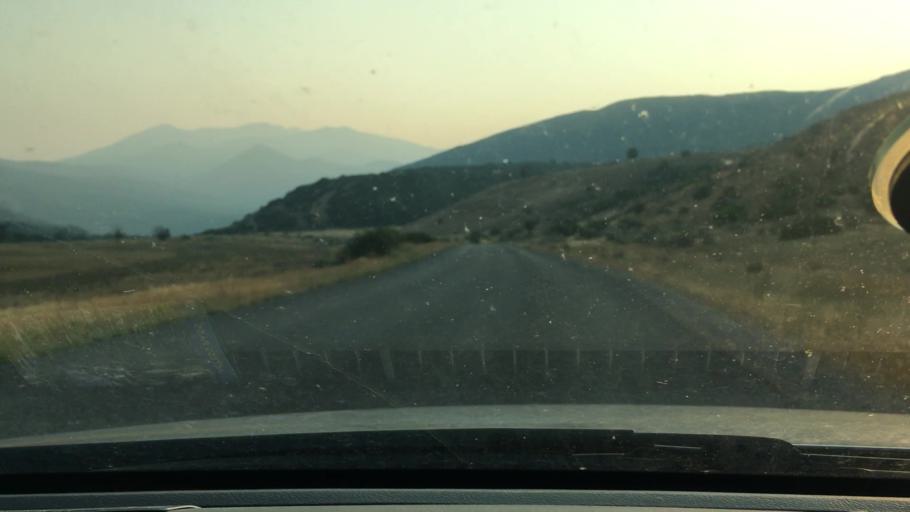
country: US
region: Utah
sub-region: Utah County
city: Mapleton
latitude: 40.0455
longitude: -111.4714
